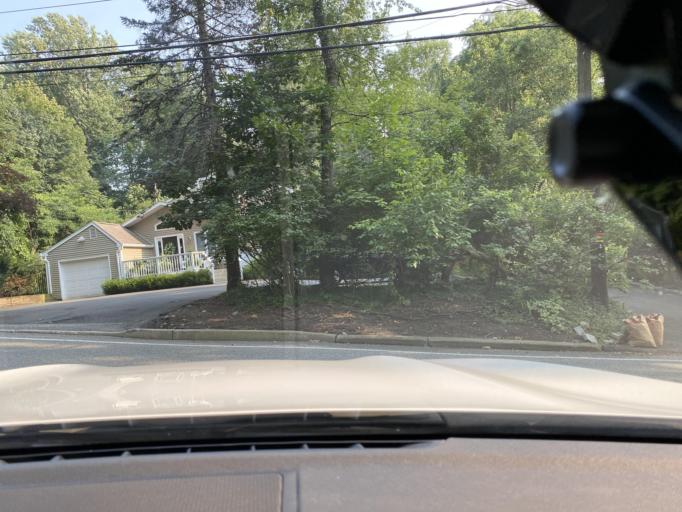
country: US
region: New Jersey
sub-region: Bergen County
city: Mahwah
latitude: 41.0946
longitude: -74.1344
